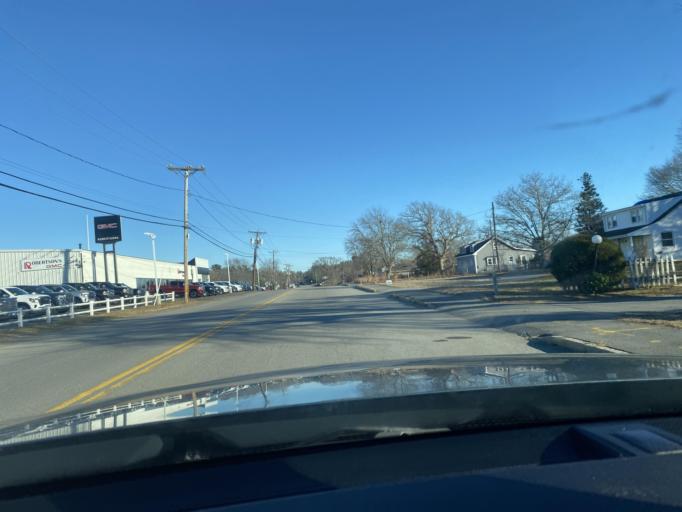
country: US
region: Massachusetts
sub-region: Plymouth County
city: Wareham Center
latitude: 41.7699
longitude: -70.7059
